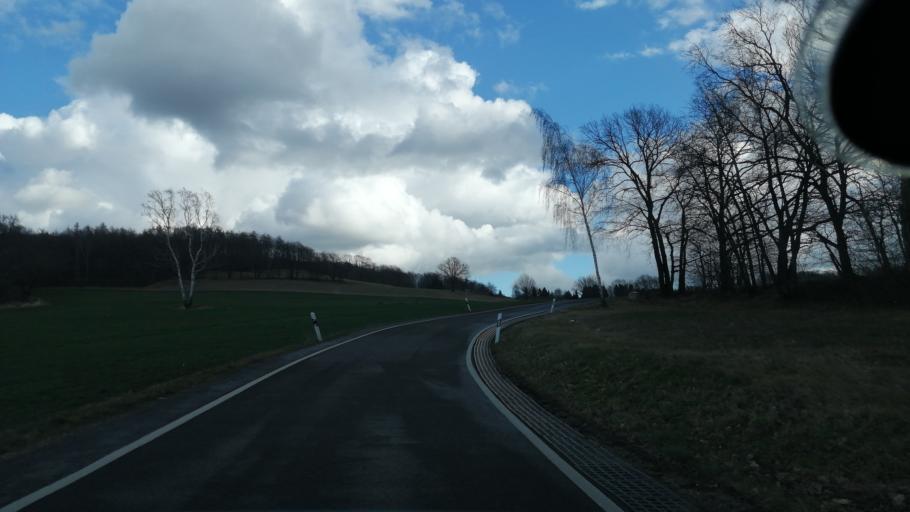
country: DE
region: Saxony
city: Grosspostwitz
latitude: 51.1425
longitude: 14.4706
